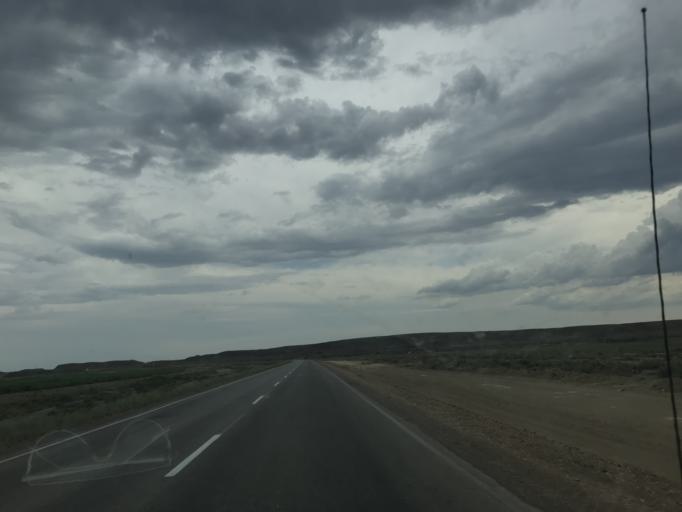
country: KZ
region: Almaty Oblysy
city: Ulken
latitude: 45.0344
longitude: 73.9855
